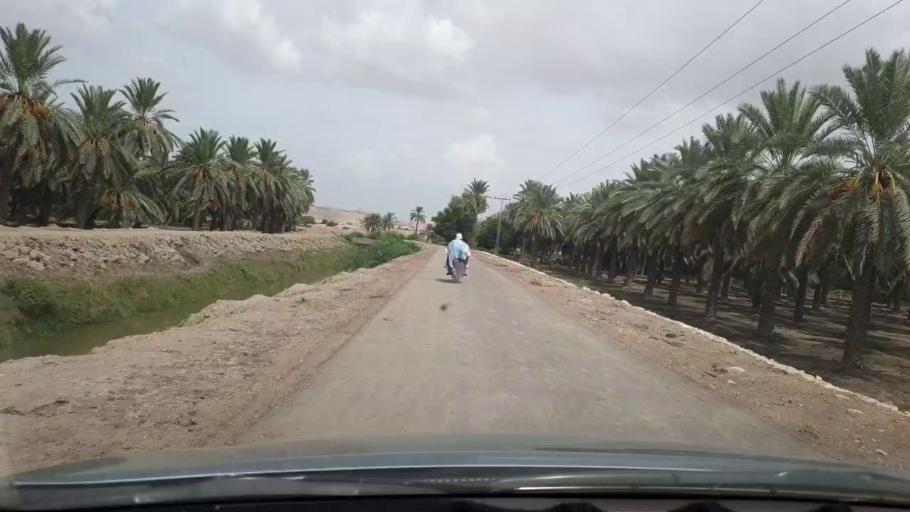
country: PK
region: Sindh
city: Khairpur
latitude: 27.4779
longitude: 68.8511
